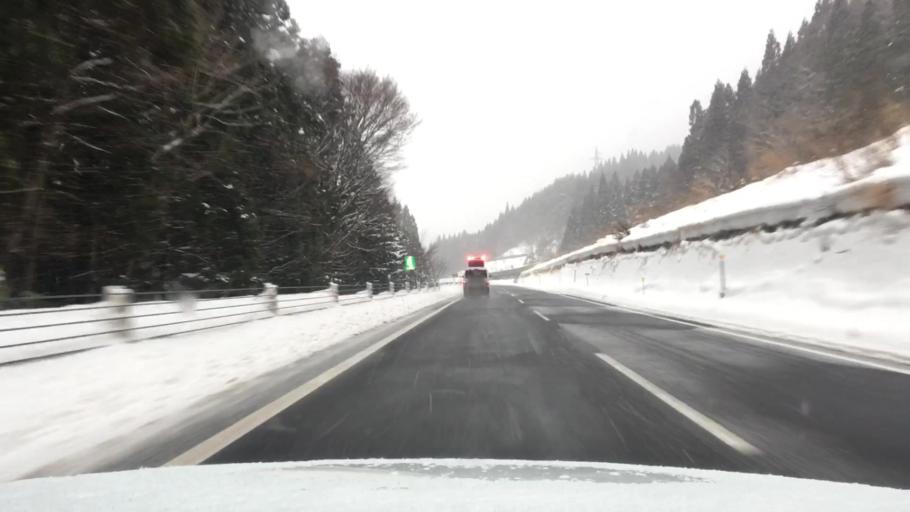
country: JP
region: Akita
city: Hanawa
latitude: 40.1434
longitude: 140.8084
